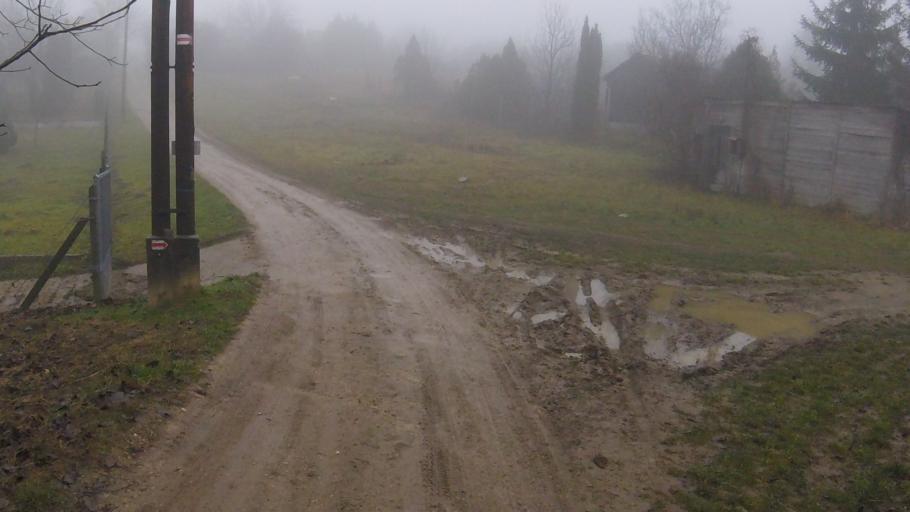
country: HU
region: Pest
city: Biatorbagy
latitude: 47.4584
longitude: 18.8377
